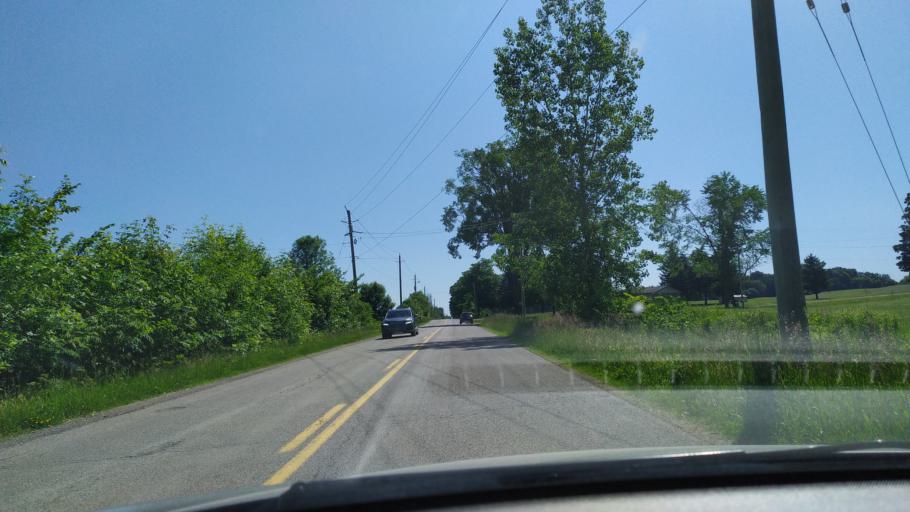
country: CA
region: Ontario
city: Waterloo
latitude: 43.4684
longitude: -80.6545
